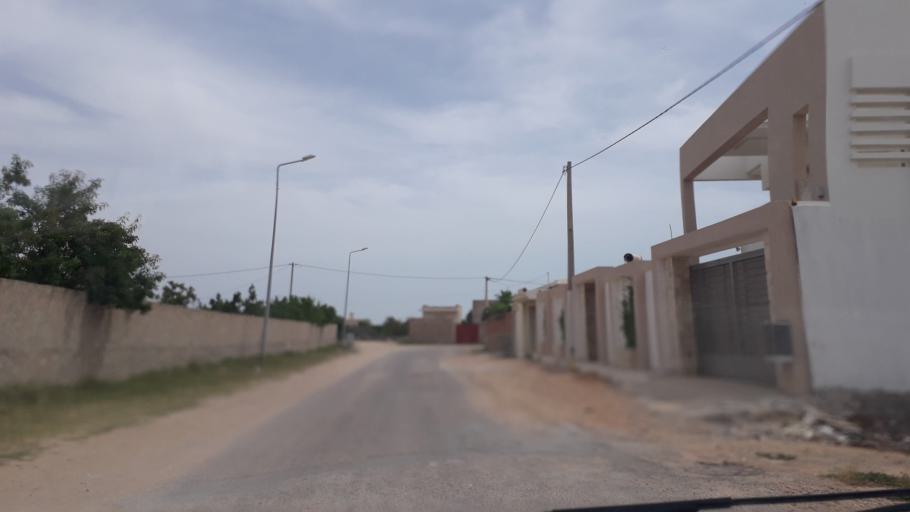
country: TN
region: Safaqis
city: Al Qarmadah
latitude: 34.8095
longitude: 10.7706
